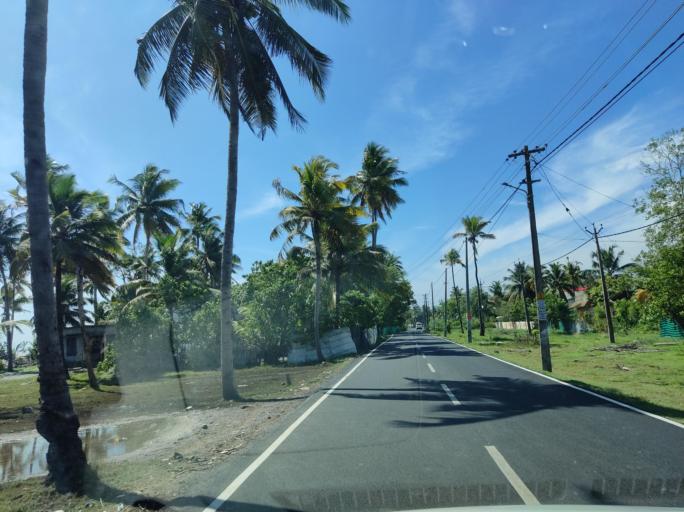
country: IN
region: Kerala
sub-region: Alappuzha
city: Kayankulam
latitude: 9.1698
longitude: 76.4483
